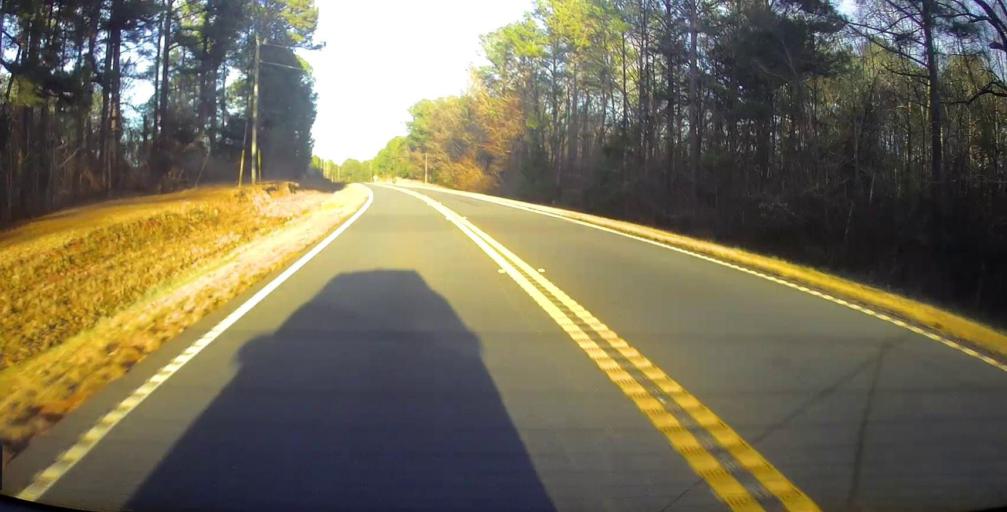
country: US
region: Georgia
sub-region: Talbot County
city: Sardis
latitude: 32.7486
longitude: -84.5821
